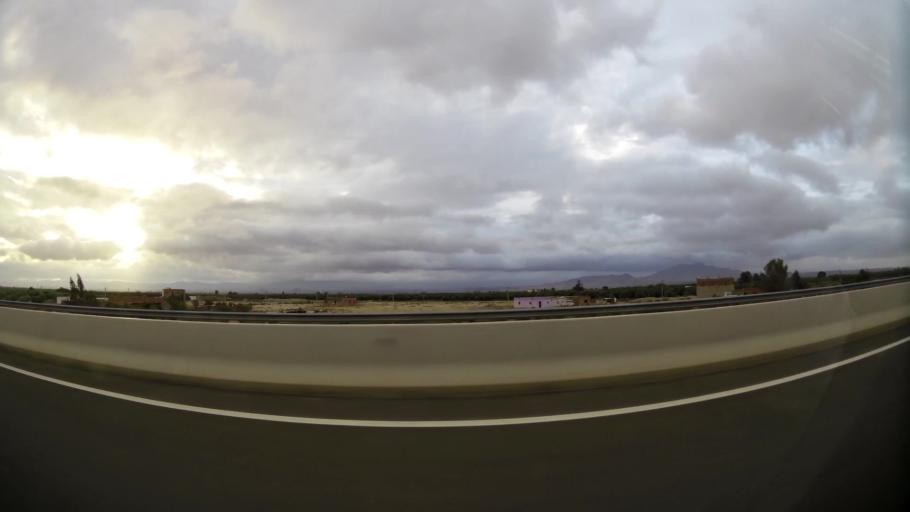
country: MA
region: Taza-Al Hoceima-Taounate
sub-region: Taza
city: Guercif
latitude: 34.3606
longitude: -3.2961
